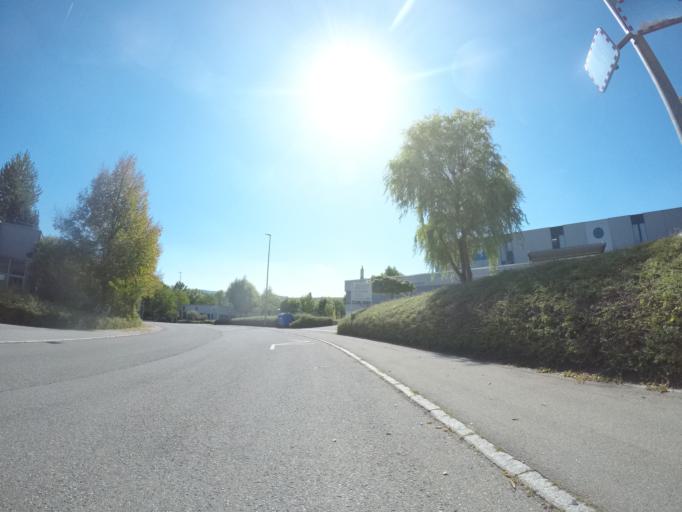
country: DE
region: Baden-Wuerttemberg
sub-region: Tuebingen Region
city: Wannweil
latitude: 48.4889
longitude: 9.1494
